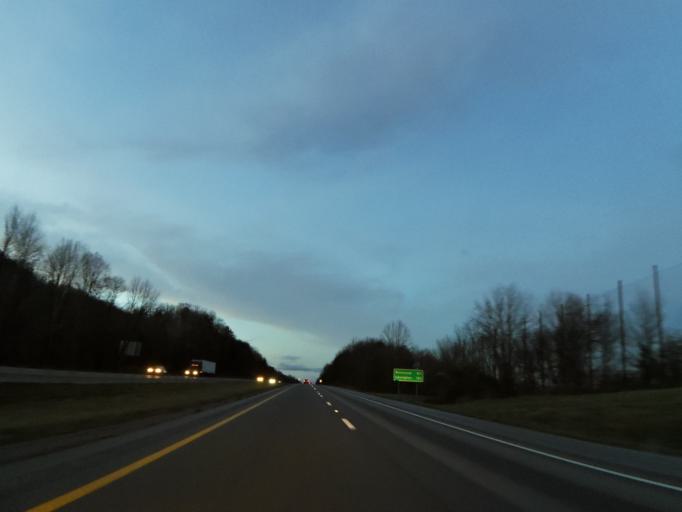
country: US
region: Kentucky
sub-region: Whitley County
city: Williamsburg
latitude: 36.7359
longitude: -84.1730
